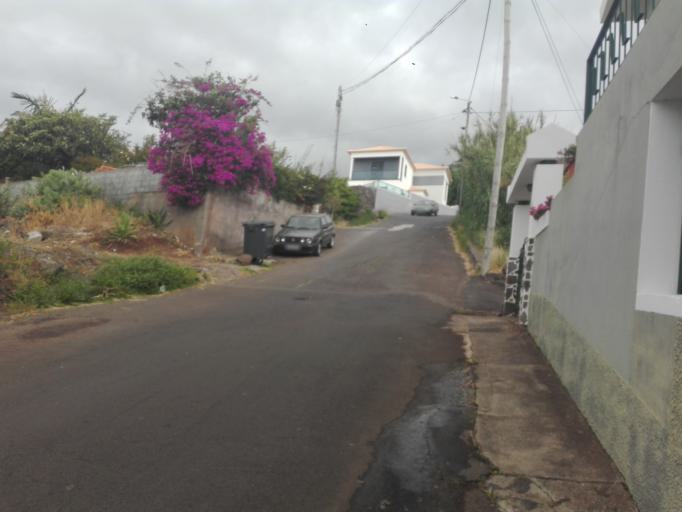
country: PT
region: Madeira
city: Canico
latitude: 32.6533
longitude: -16.8282
